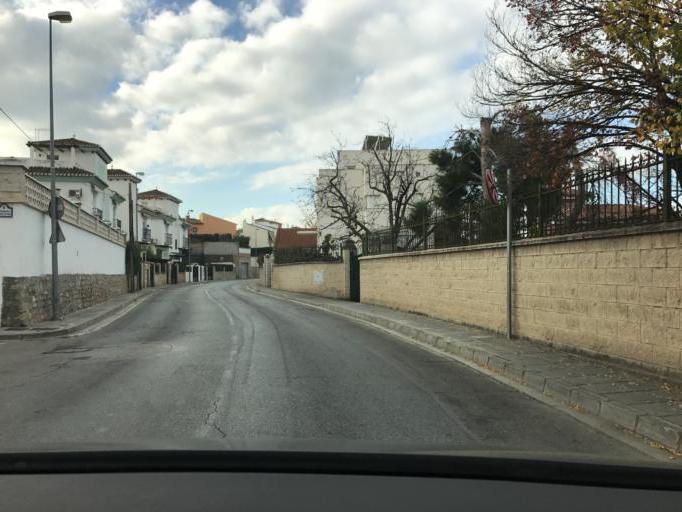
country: ES
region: Andalusia
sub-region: Provincia de Granada
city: Ogijares
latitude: 37.1257
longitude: -3.6075
